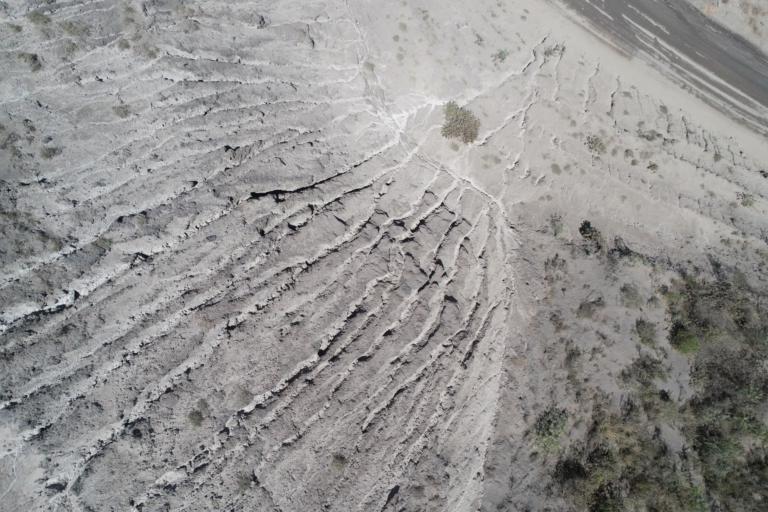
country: BO
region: La Paz
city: La Paz
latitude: -16.6133
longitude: -68.0598
